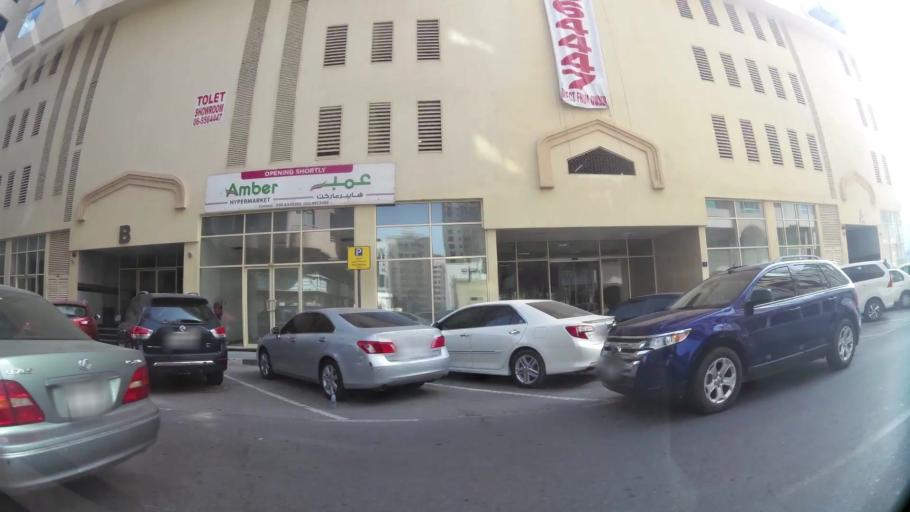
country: AE
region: Ash Shariqah
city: Sharjah
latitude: 25.3415
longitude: 55.3915
